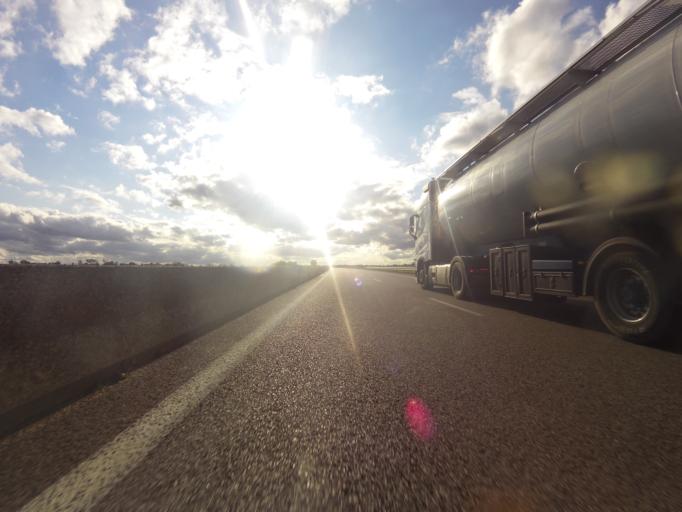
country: FR
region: Picardie
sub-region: Departement de la Somme
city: Beaucamps-le-Vieux
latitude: 49.8059
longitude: 1.8228
